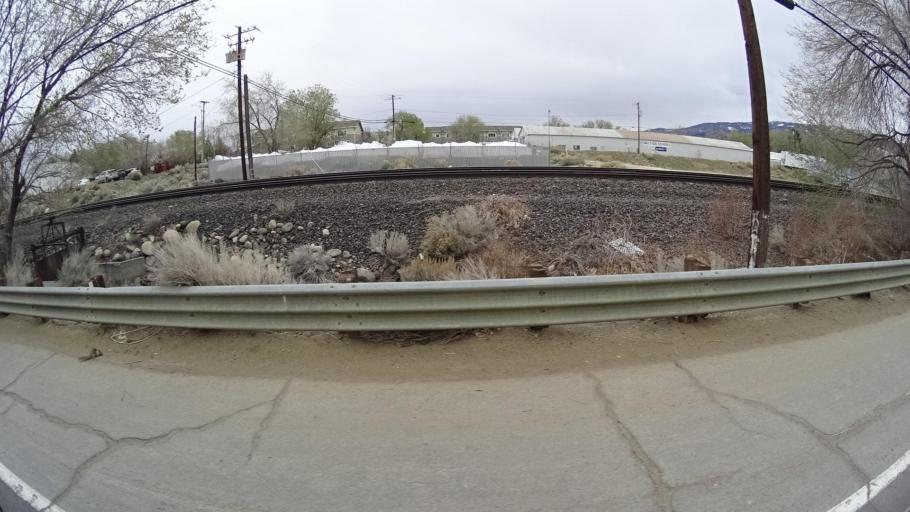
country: US
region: Nevada
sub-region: Washoe County
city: Reno
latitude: 39.5205
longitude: -119.8445
